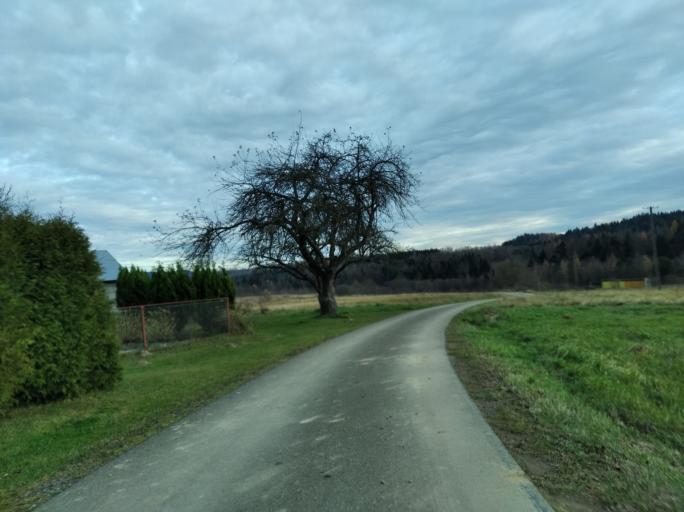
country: PL
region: Subcarpathian Voivodeship
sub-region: Powiat brzozowski
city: Domaradz
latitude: 49.7820
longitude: 21.9132
